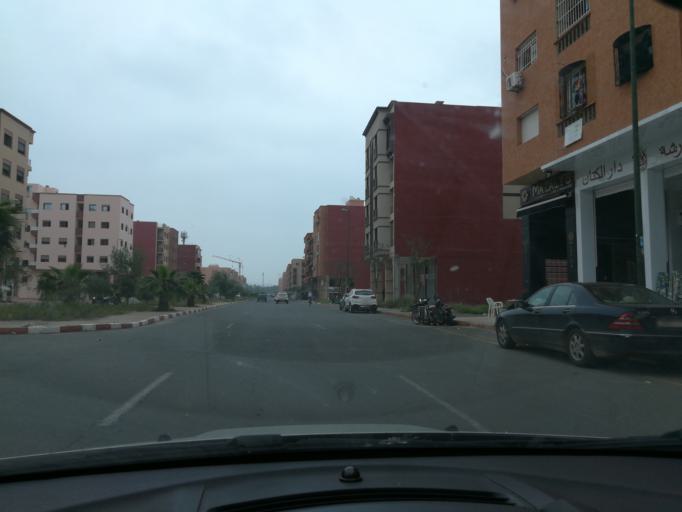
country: MA
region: Marrakech-Tensift-Al Haouz
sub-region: Marrakech
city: Marrakesh
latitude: 31.6730
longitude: -8.0273
